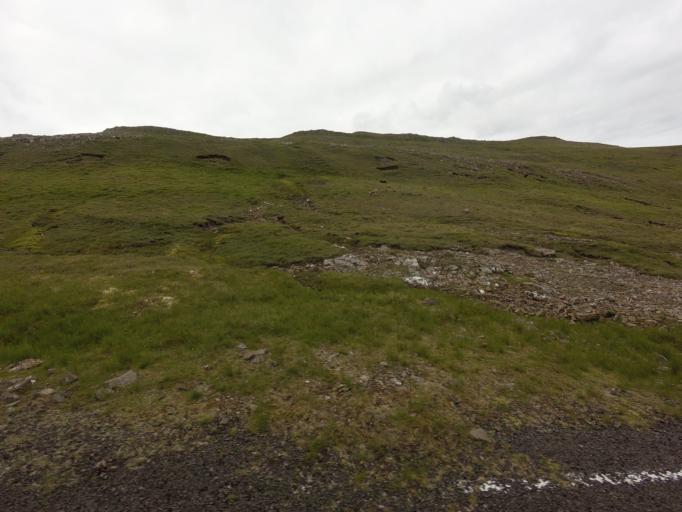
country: FO
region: Suduroy
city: Vagur
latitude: 61.4398
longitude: -6.7482
